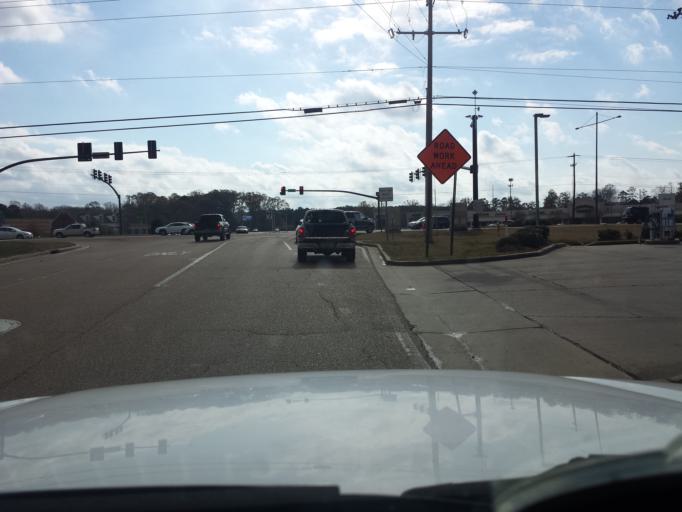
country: US
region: Mississippi
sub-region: Rankin County
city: Flowood
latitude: 32.3387
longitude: -90.0933
